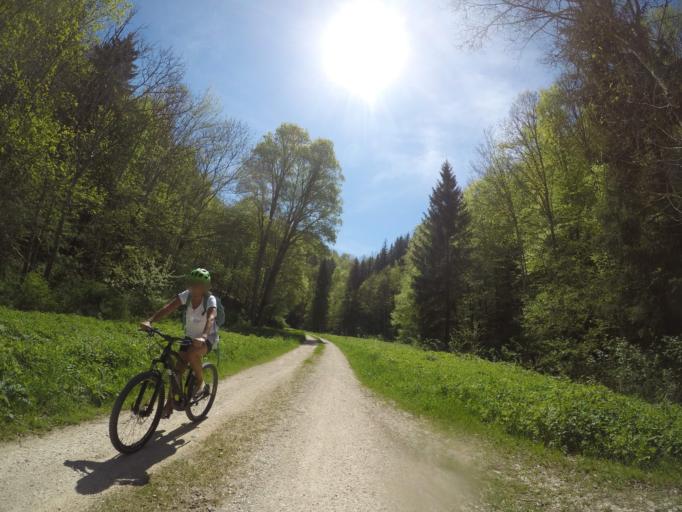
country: DE
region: Baden-Wuerttemberg
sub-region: Tuebingen Region
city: Schelklingen
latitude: 48.4151
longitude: 9.7174
